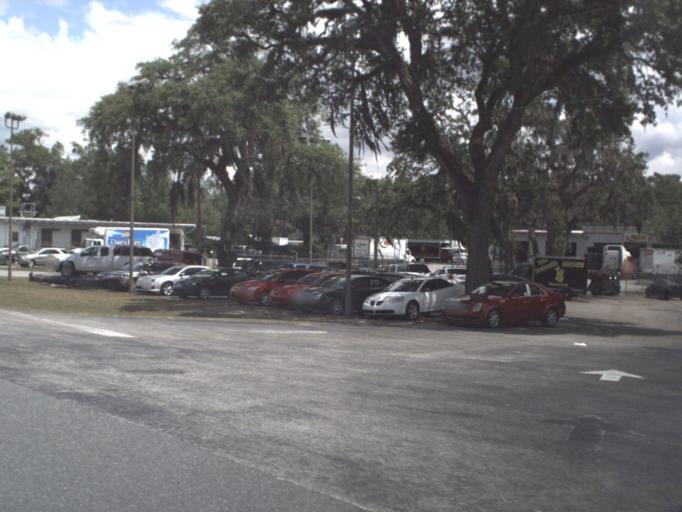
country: US
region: Florida
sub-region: Marion County
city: Ocala
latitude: 29.2092
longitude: -82.1424
